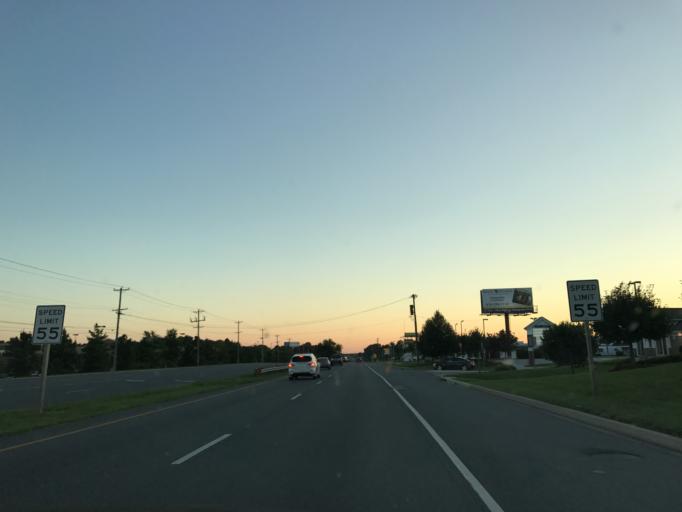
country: US
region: Maryland
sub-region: Cecil County
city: Elkton
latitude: 39.6055
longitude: -75.7907
